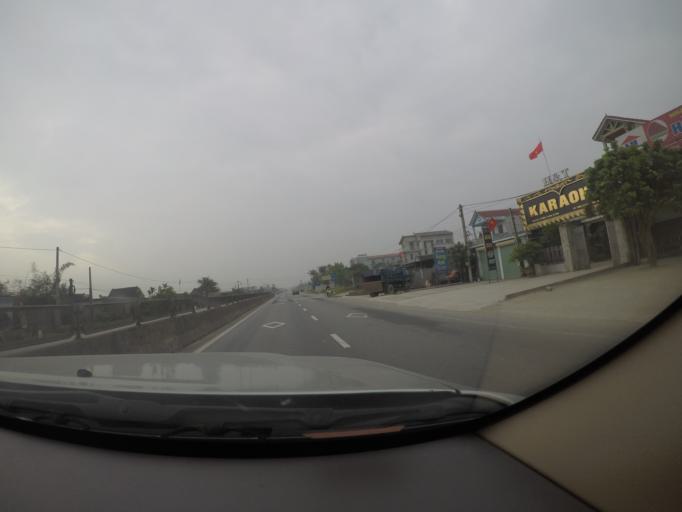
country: VN
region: Ha Tinh
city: Ky Anh
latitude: 18.1683
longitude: 106.2271
